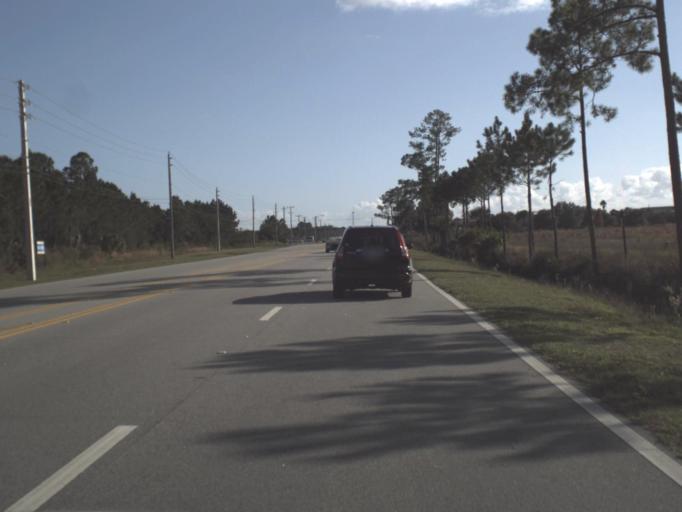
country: US
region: Florida
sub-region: Volusia County
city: Holly Hill
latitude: 29.2281
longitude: -81.0952
